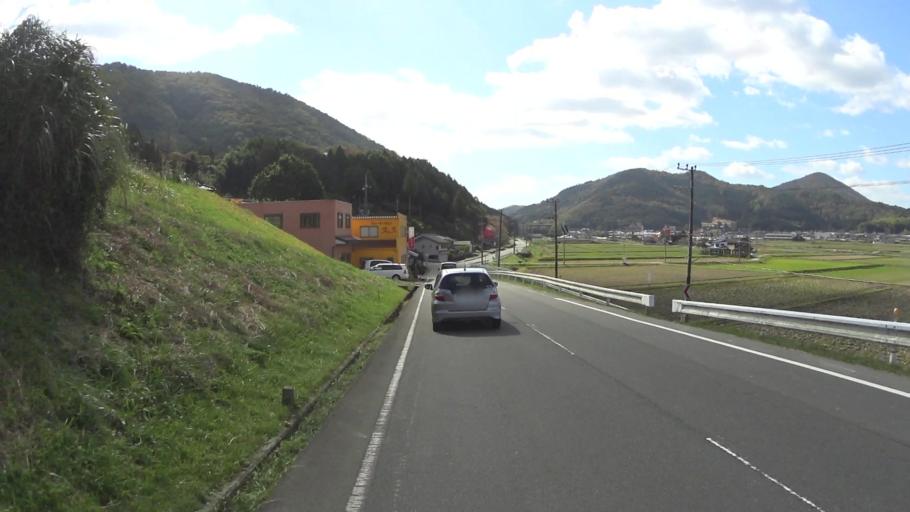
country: JP
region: Kyoto
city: Kameoka
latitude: 35.1603
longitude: 135.4348
